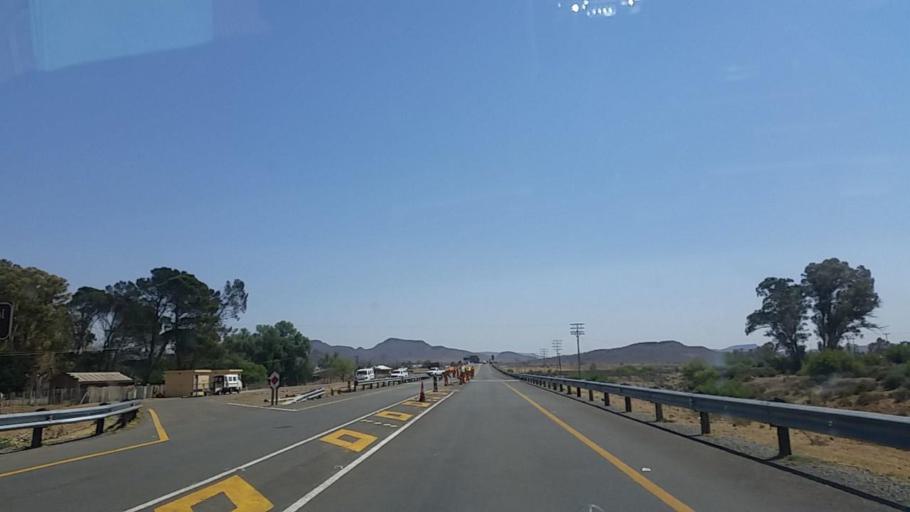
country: ZA
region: Eastern Cape
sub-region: Chris Hani District Municipality
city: Middelburg
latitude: -31.4986
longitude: 25.0200
